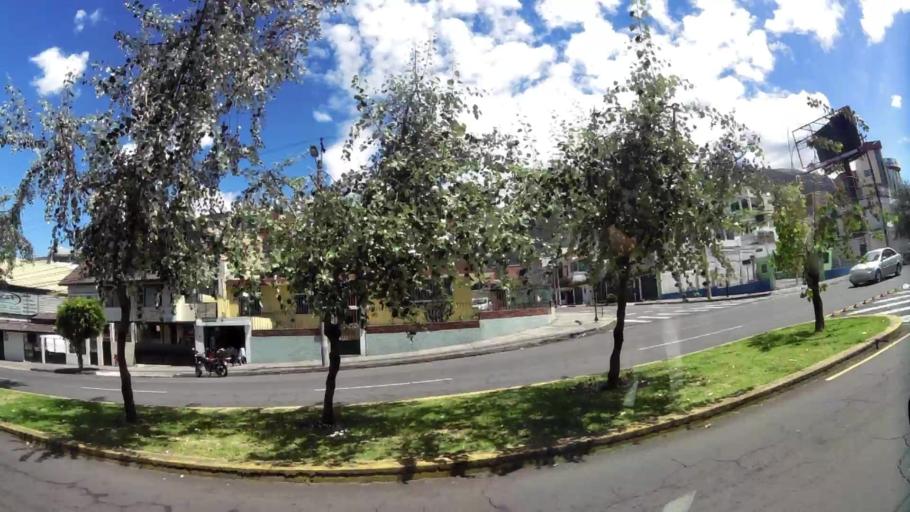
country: EC
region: Pichincha
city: Quito
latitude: -0.1776
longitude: -78.4920
